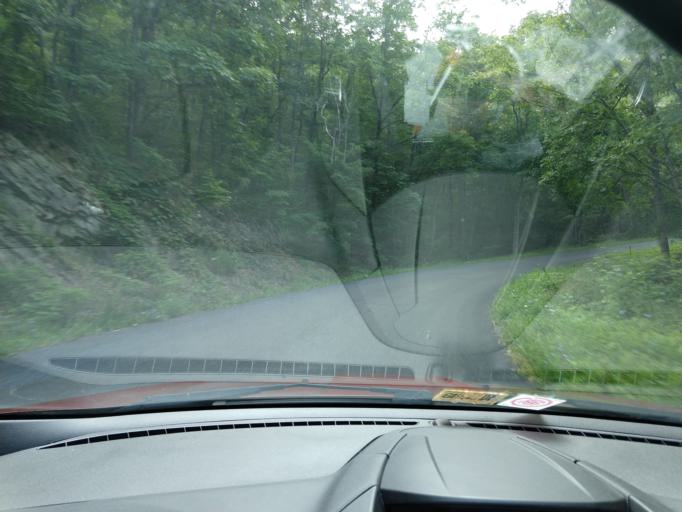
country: US
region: Virginia
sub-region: City of Covington
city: Covington
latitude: 37.9162
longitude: -80.0753
